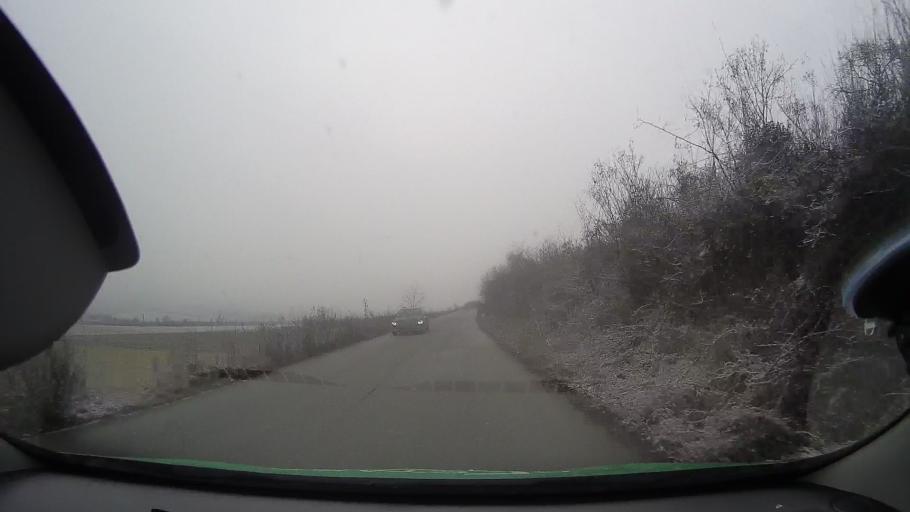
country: RO
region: Alba
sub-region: Comuna Noslac
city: Noslac
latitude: 46.3685
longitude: 23.9285
